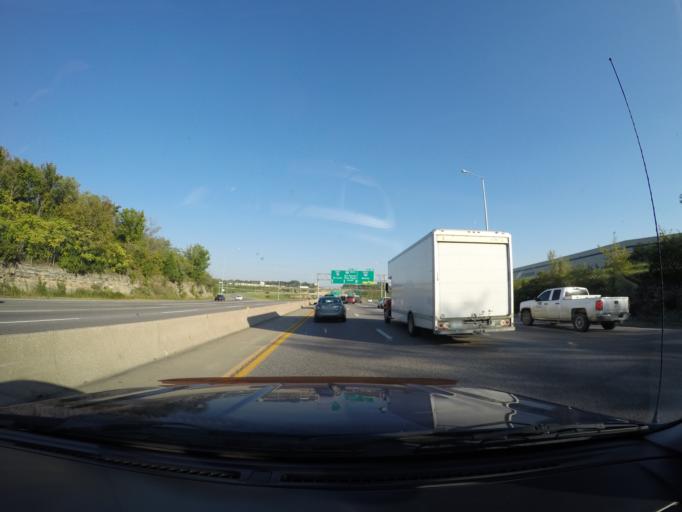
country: US
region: Missouri
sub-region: Jackson County
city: Raytown
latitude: 39.0614
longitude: -94.4952
